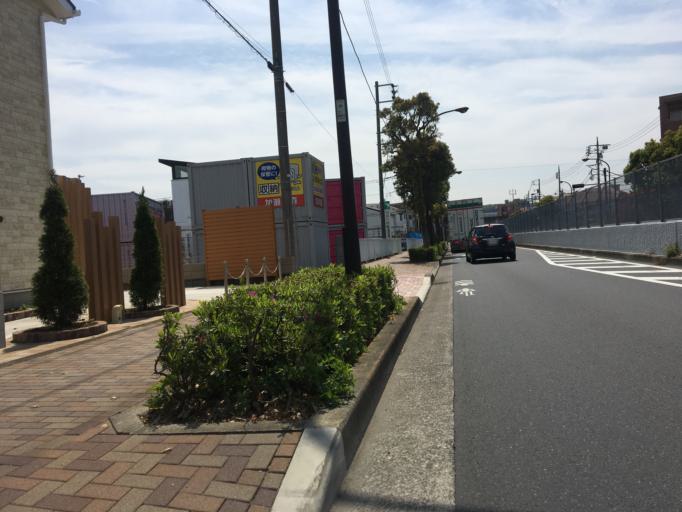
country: JP
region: Tokyo
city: Chofugaoka
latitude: 35.6448
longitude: 139.5093
